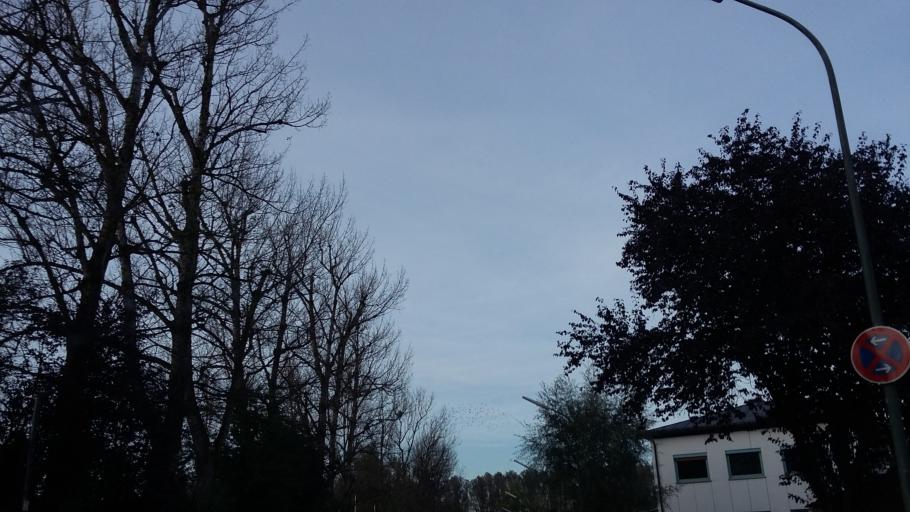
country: DE
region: Bavaria
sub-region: Upper Bavaria
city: Starnberg
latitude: 48.0028
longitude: 11.3517
